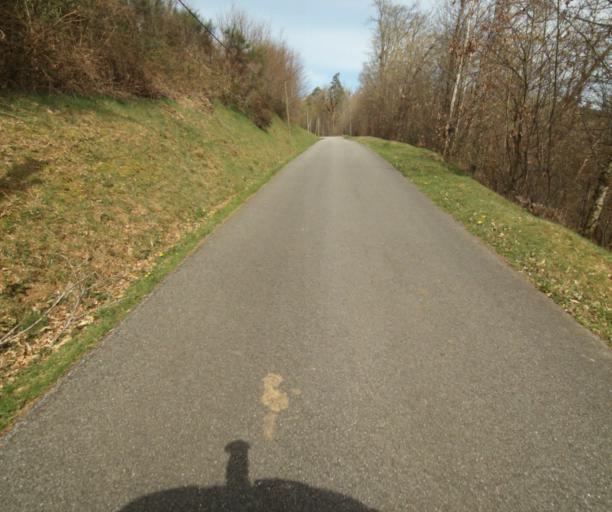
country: FR
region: Limousin
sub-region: Departement de la Correze
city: Naves
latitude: 45.3291
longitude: 1.8037
